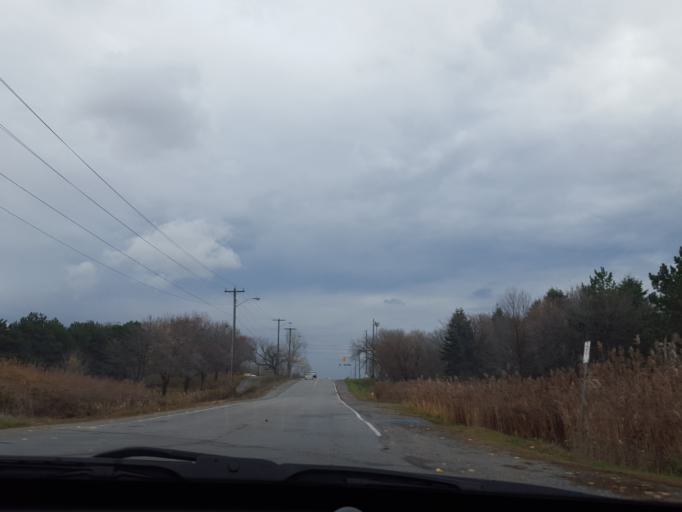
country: CA
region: Ontario
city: Ajax
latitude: 43.8150
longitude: -79.0625
